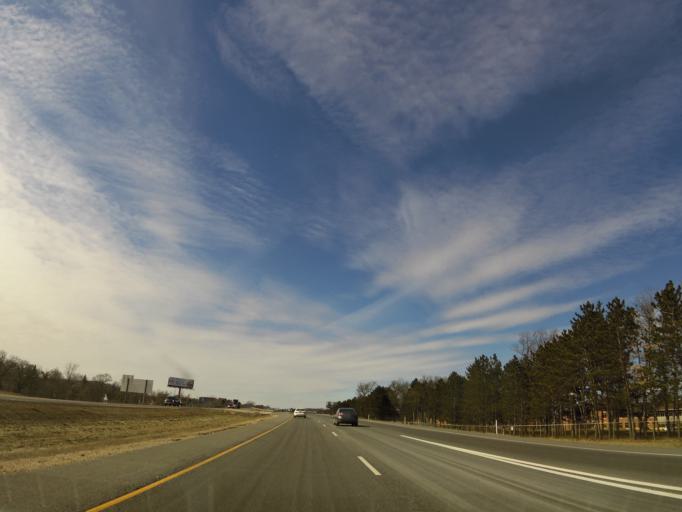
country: US
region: Wisconsin
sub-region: Juneau County
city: New Lisbon
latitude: 43.9237
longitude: -90.2664
